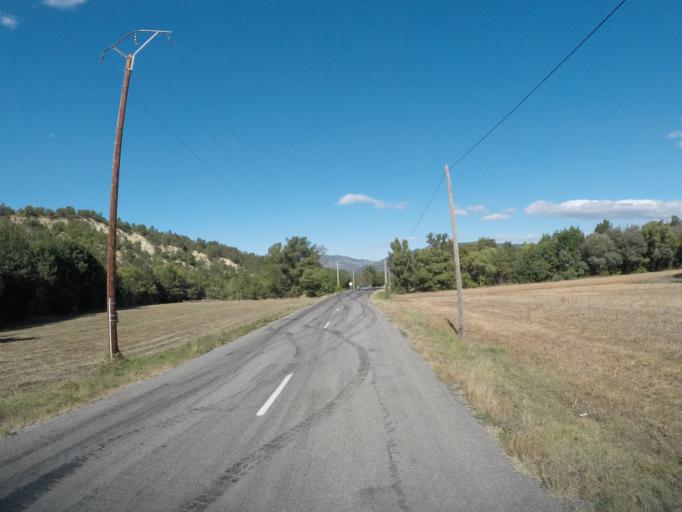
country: FR
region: Provence-Alpes-Cote d'Azur
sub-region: Departement des Alpes-de-Haute-Provence
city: Mallemoisson
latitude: 44.0381
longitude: 6.1704
